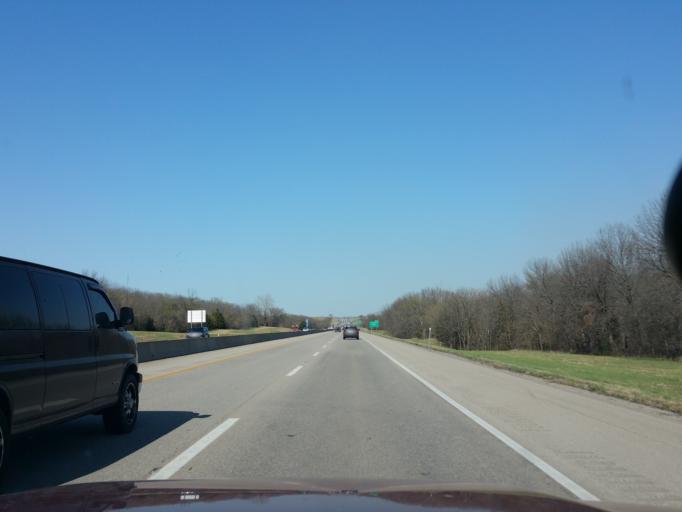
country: US
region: Kansas
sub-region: Leavenworth County
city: Tonganoxie
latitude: 39.0290
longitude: -95.1194
